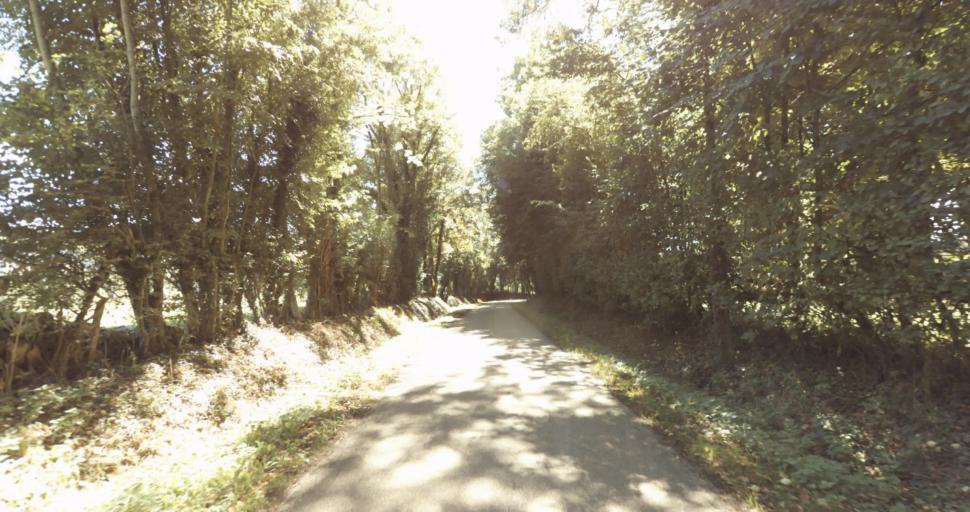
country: FR
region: Lower Normandy
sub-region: Departement de l'Orne
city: Gace
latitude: 48.7938
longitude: 0.2881
